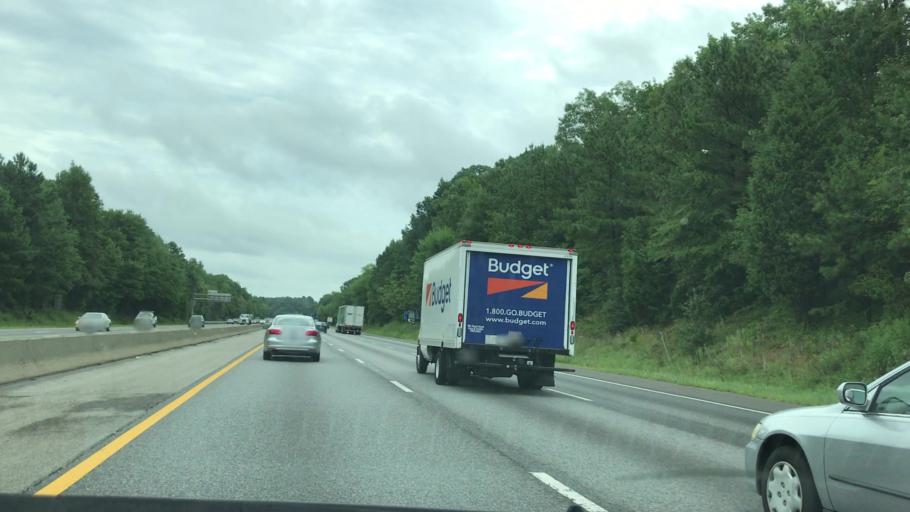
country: US
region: Virginia
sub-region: City of Colonial Heights
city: Colonial Heights
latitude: 37.2700
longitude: -77.3942
